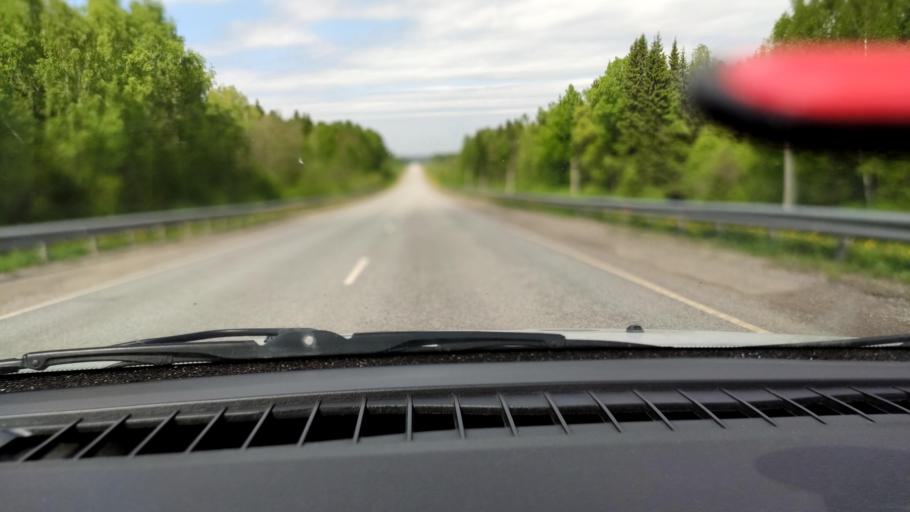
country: RU
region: Perm
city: Bershet'
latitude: 57.7601
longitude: 56.3615
